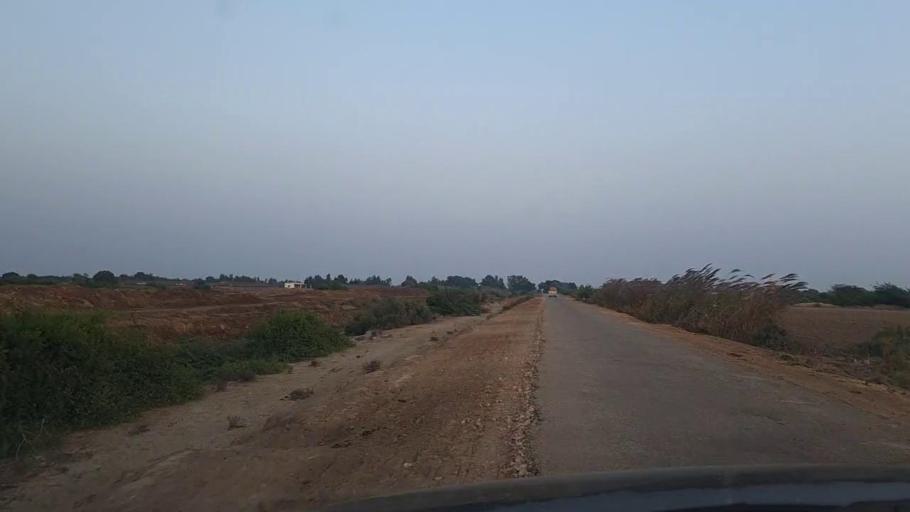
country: PK
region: Sindh
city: Mirpur Sakro
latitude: 24.6287
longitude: 67.6454
